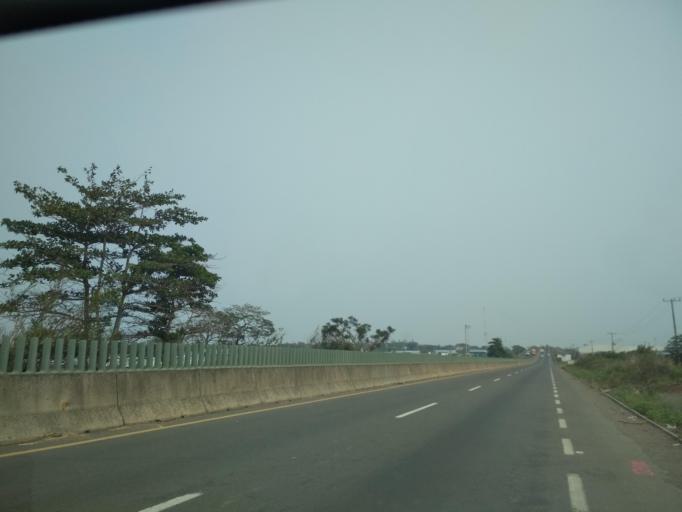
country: MX
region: Veracruz
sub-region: Veracruz
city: Delfino Victoria (Santa Fe)
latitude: 19.1722
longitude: -96.2679
